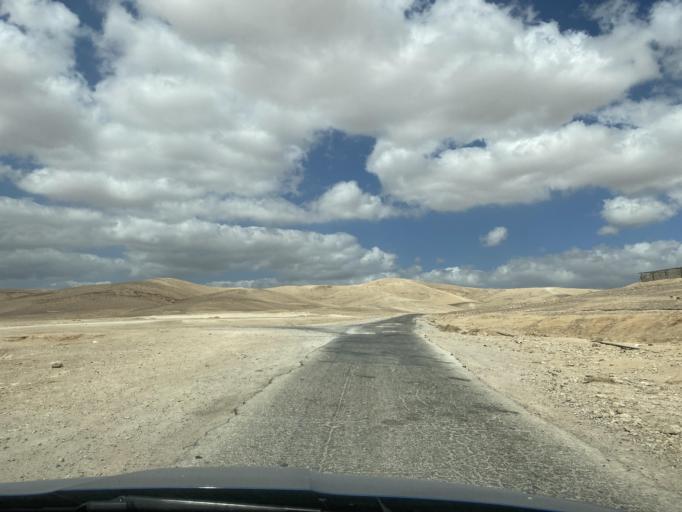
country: PS
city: `Arab ar Rashaydah
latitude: 31.5327
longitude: 35.2778
